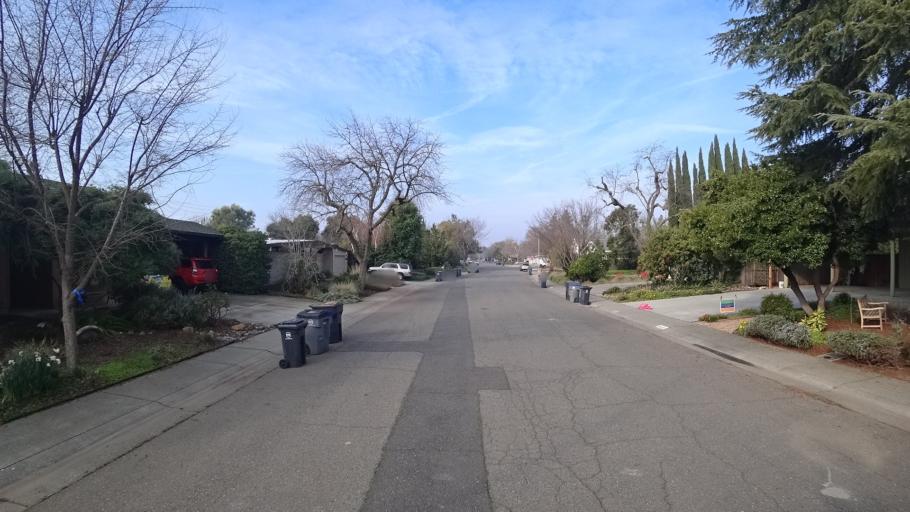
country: US
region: California
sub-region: Yolo County
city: Davis
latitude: 38.5554
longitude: -121.7613
